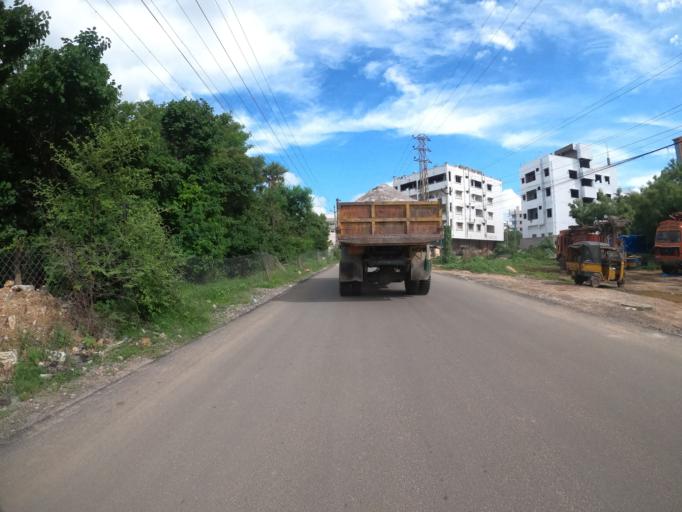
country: IN
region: Telangana
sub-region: Hyderabad
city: Hyderabad
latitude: 17.3540
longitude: 78.3890
